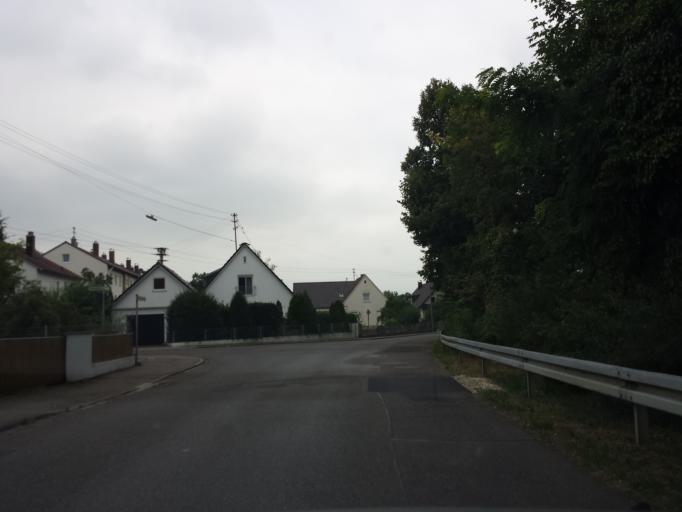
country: DE
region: Bavaria
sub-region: Swabia
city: Wasserburg
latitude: 48.4425
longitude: 10.2696
